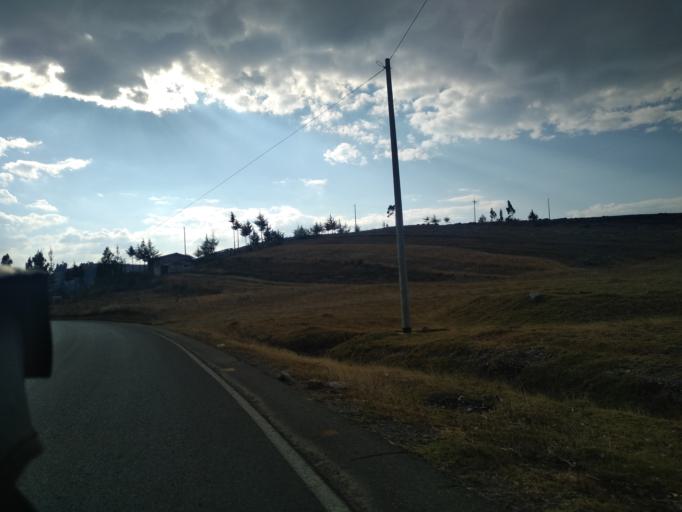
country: PE
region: Cajamarca
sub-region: Provincia de Cajamarca
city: Llacanora
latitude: -7.1434
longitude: -78.4025
